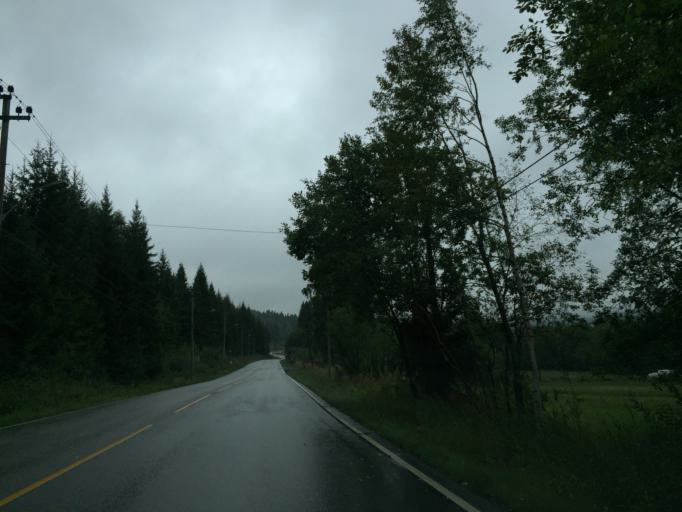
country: NO
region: Akershus
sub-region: Baerum
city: Lysaker
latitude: 59.9982
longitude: 10.6199
